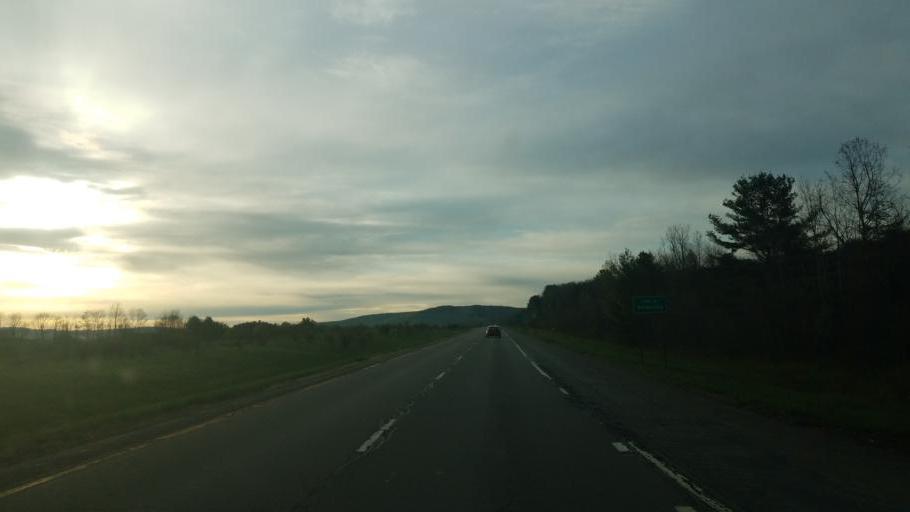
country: US
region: New York
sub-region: Allegany County
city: Belmont
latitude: 42.2981
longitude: -78.0050
